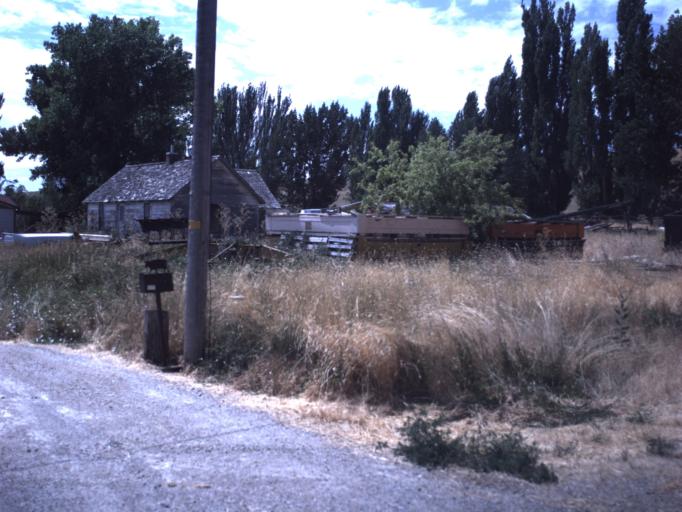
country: US
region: Utah
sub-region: Box Elder County
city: Tremonton
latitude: 41.6723
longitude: -112.2967
